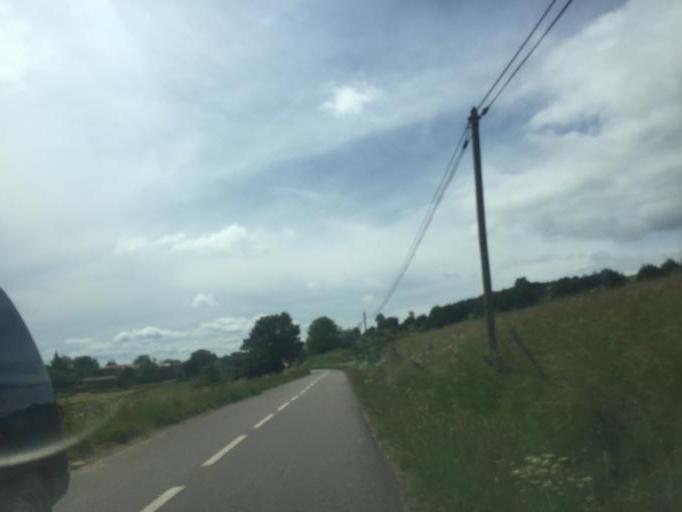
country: FR
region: Rhone-Alpes
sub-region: Departement de l'Ardeche
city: Saint-Priest
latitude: 44.6789
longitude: 4.5519
